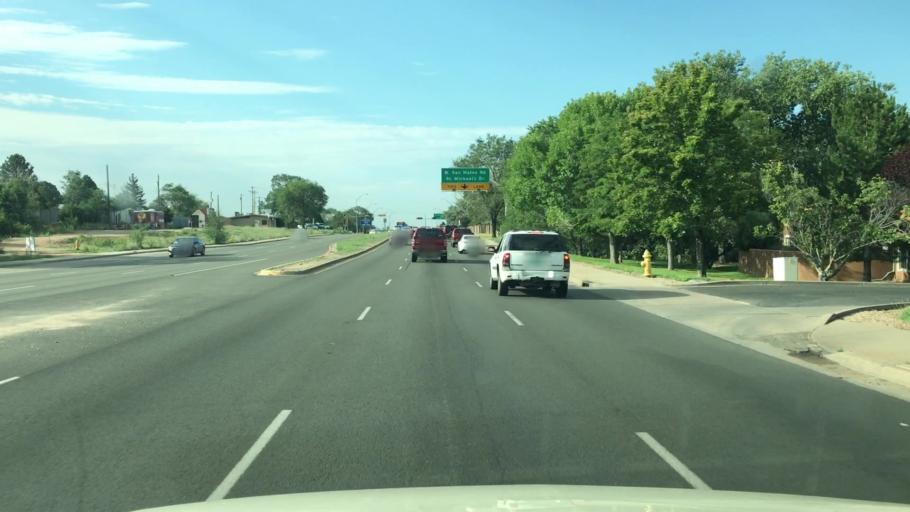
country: US
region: New Mexico
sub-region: Santa Fe County
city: Santa Fe
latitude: 35.6646
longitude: -105.9564
